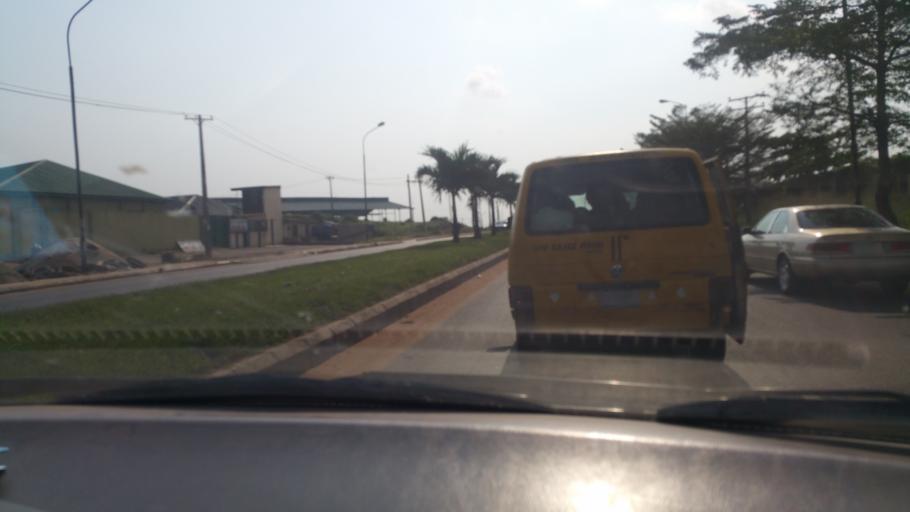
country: NG
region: Lagos
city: Ikotun
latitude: 6.5731
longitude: 3.2549
